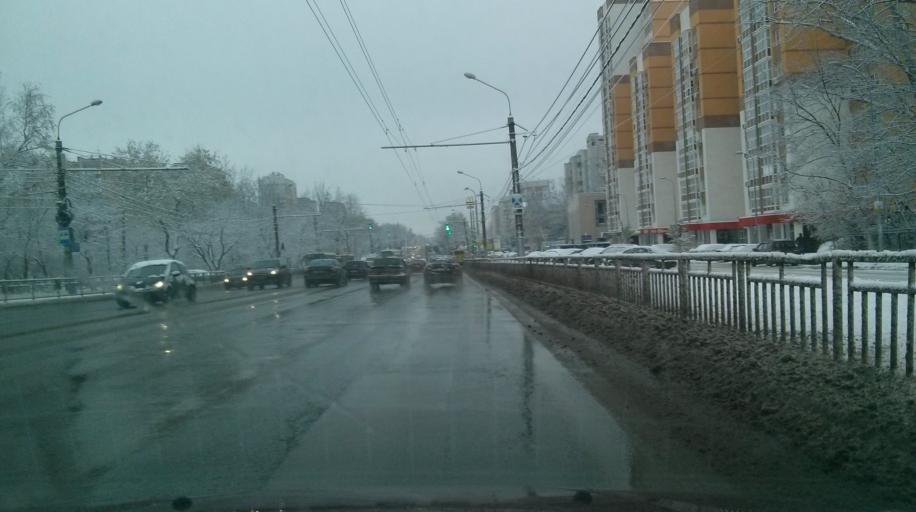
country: RU
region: Nizjnij Novgorod
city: Nizhniy Novgorod
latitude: 56.2374
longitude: 43.9561
